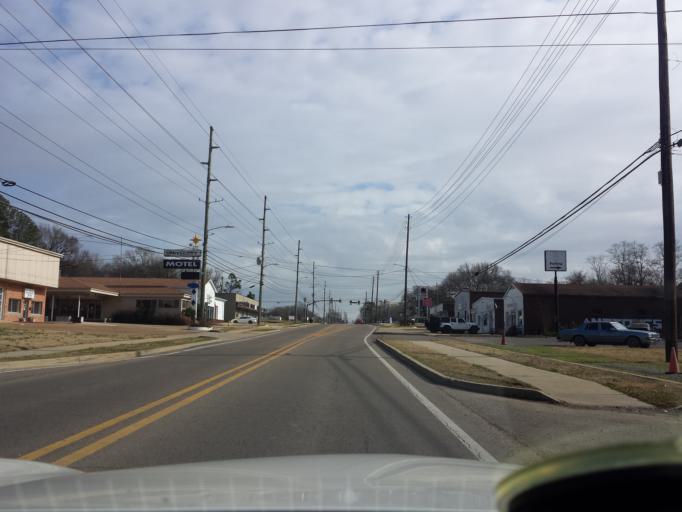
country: US
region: Mississippi
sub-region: Oktibbeha County
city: Starkville
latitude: 33.4660
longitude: -88.8184
